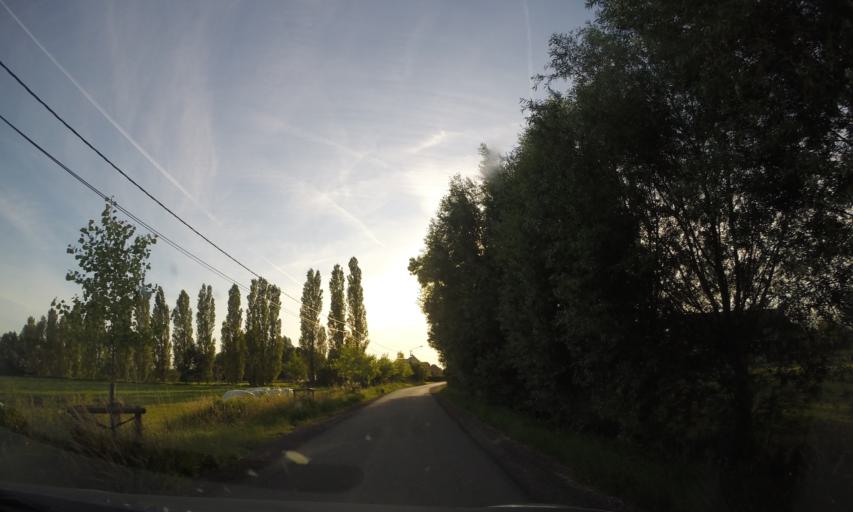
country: BE
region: Flanders
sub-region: Provincie Oost-Vlaanderen
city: Aalter
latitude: 51.1183
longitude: 3.4849
